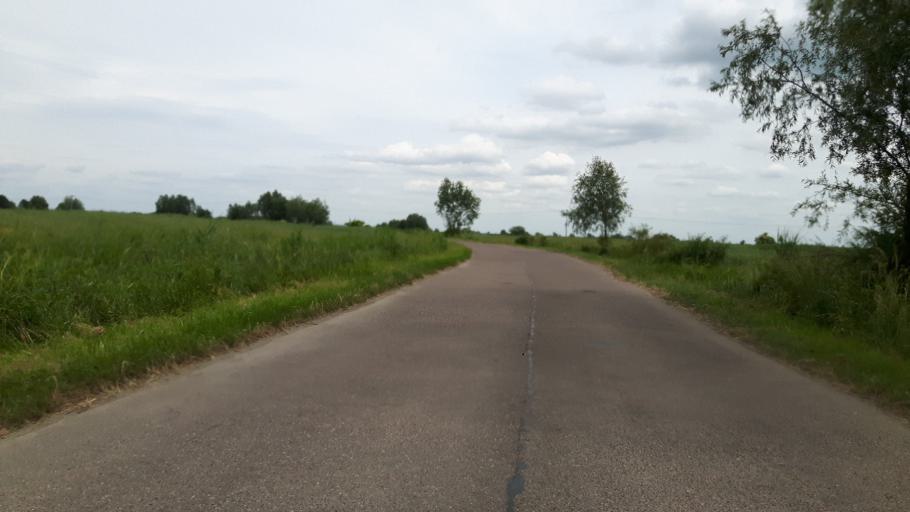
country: PL
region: Pomeranian Voivodeship
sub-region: Powiat nowodworski
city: Sztutowo
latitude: 54.2695
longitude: 19.1773
